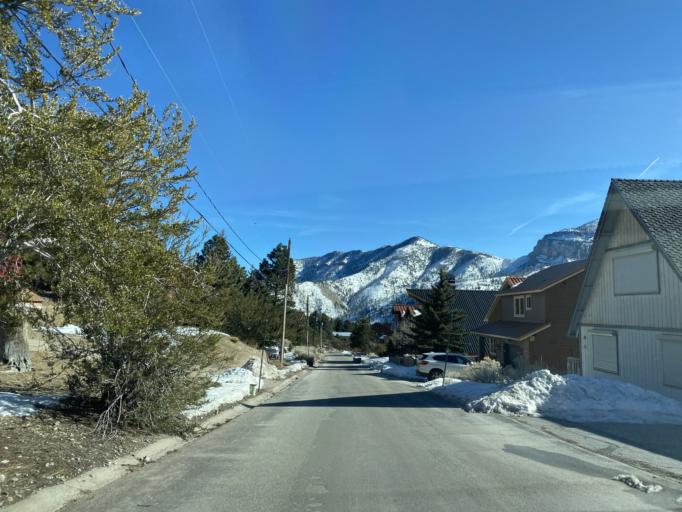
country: US
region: Nevada
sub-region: Nye County
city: Pahrump
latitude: 36.2644
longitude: -115.6557
